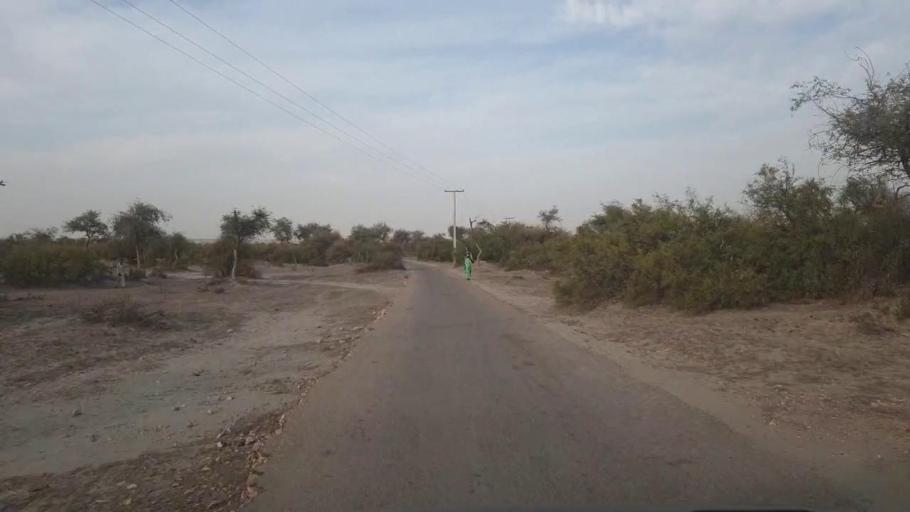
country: PK
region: Sindh
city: Nabisar
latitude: 25.1045
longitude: 69.6754
